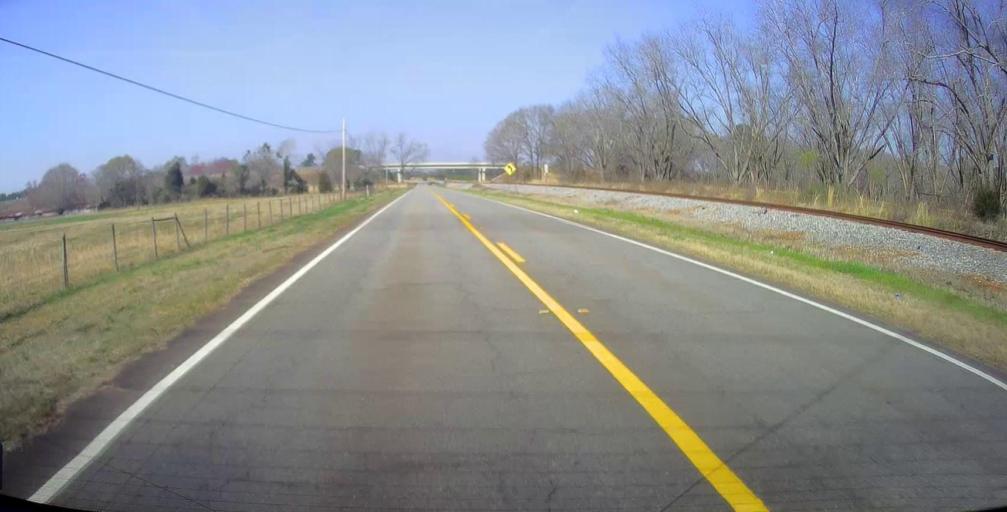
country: US
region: Georgia
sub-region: Jones County
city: Gray
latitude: 33.0251
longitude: -83.5367
